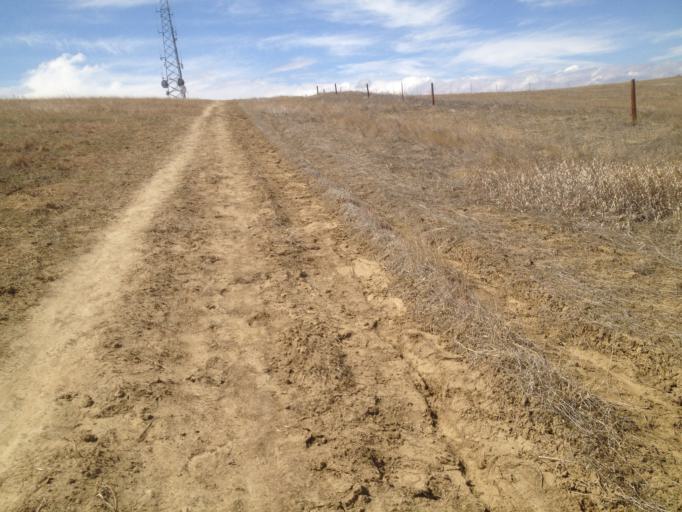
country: US
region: Colorado
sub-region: Boulder County
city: Gunbarrel
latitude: 40.0653
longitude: -105.1538
